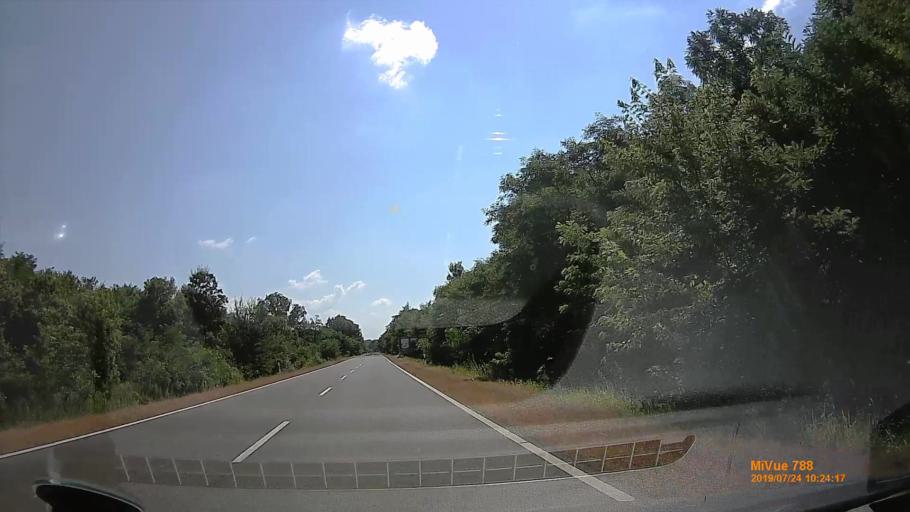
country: HU
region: Szabolcs-Szatmar-Bereg
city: Vasarosnameny
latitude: 48.1517
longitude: 22.3829
